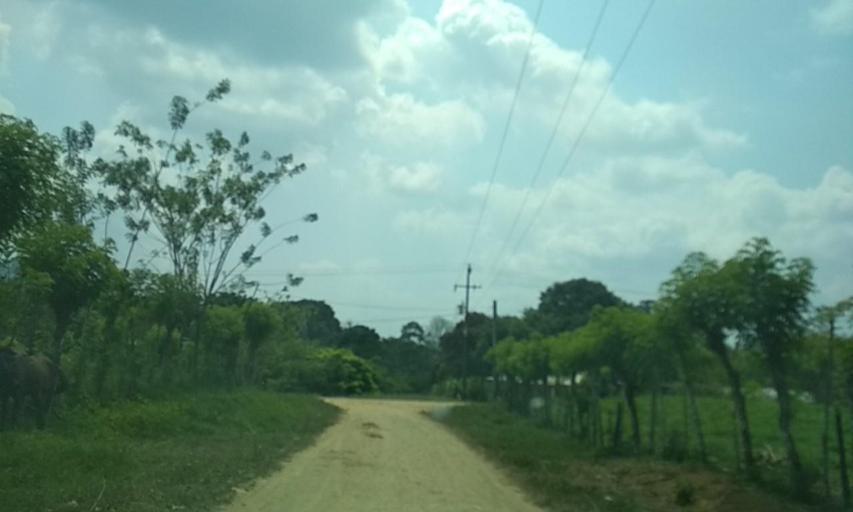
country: MX
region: Chiapas
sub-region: Tecpatan
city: Raudales Malpaso
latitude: 17.3477
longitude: -93.9640
